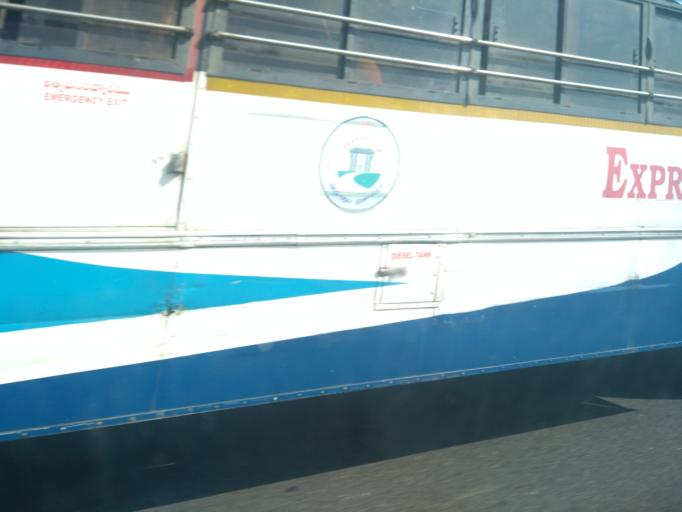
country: IN
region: Telangana
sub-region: Mahbubnagar
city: Wanparti
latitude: 16.4456
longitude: 77.9380
